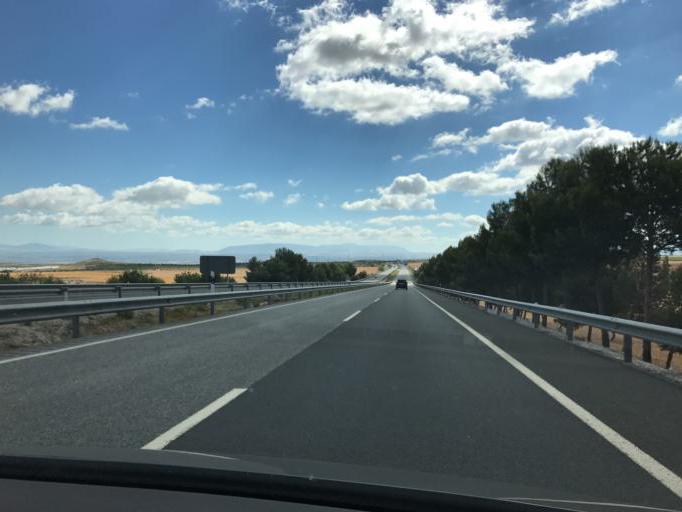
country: ES
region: Andalusia
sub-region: Provincia de Granada
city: Zujar
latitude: 37.4915
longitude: -2.8367
